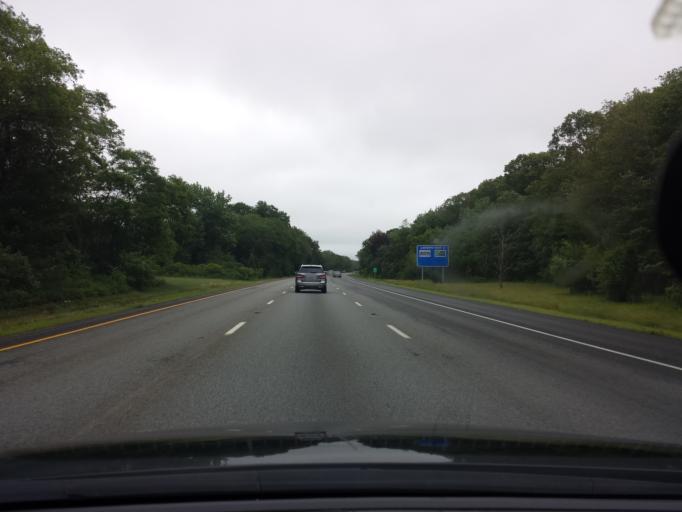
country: US
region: Massachusetts
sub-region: Bristol County
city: Ocean Grove
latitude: 41.7677
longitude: -71.2418
